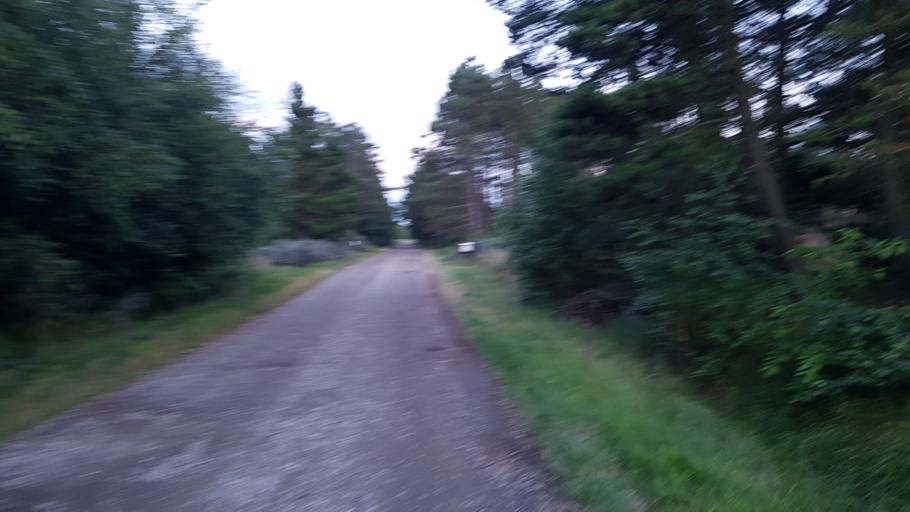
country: DE
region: Schleswig-Holstein
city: List
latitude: 55.0912
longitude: 8.5270
